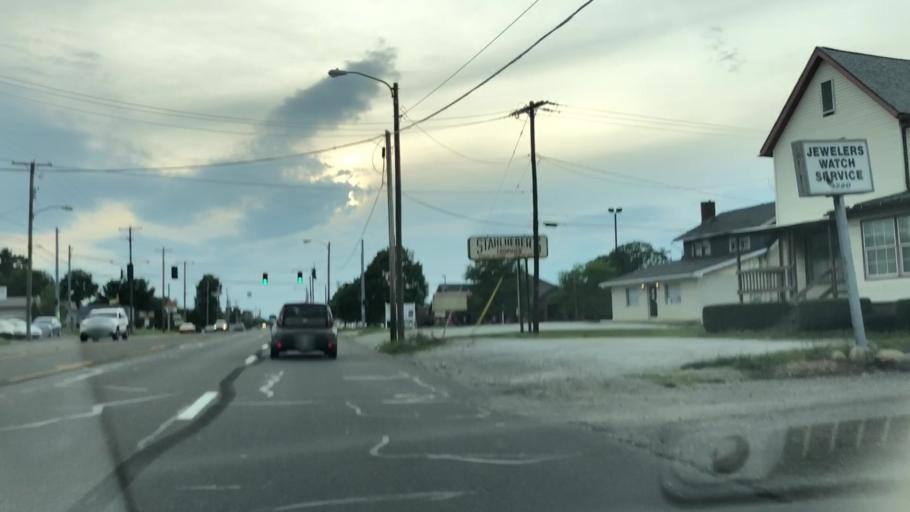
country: US
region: Ohio
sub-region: Stark County
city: Genoa
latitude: 40.7930
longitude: -81.4547
